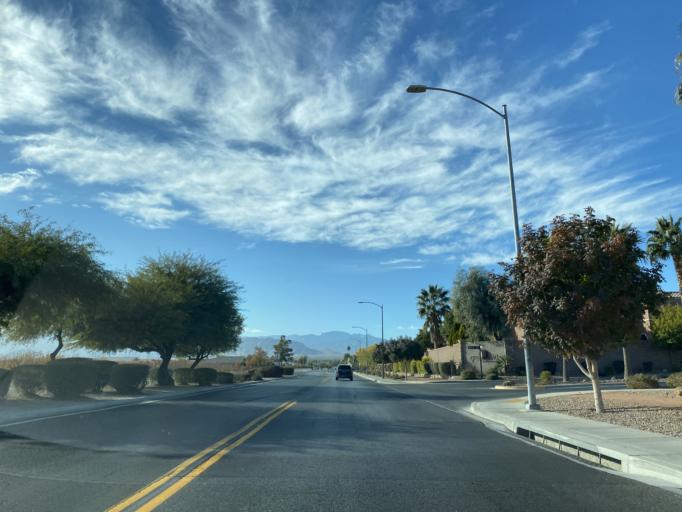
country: US
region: Nevada
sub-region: Clark County
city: North Las Vegas
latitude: 36.3053
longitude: -115.2485
